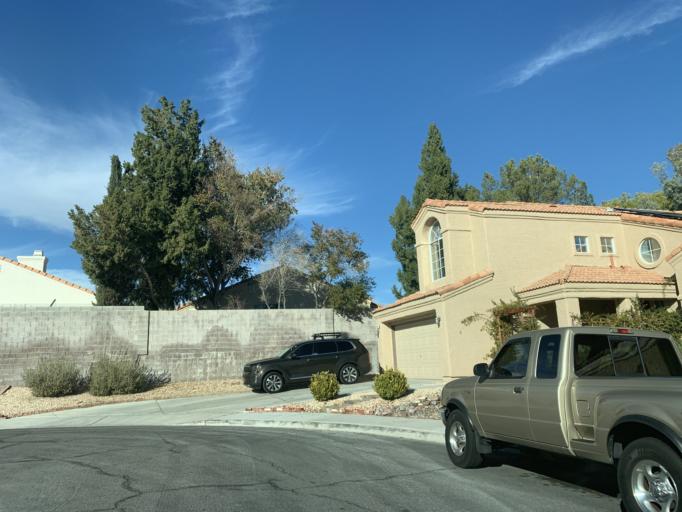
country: US
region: Nevada
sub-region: Clark County
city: Summerlin South
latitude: 36.1316
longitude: -115.3070
